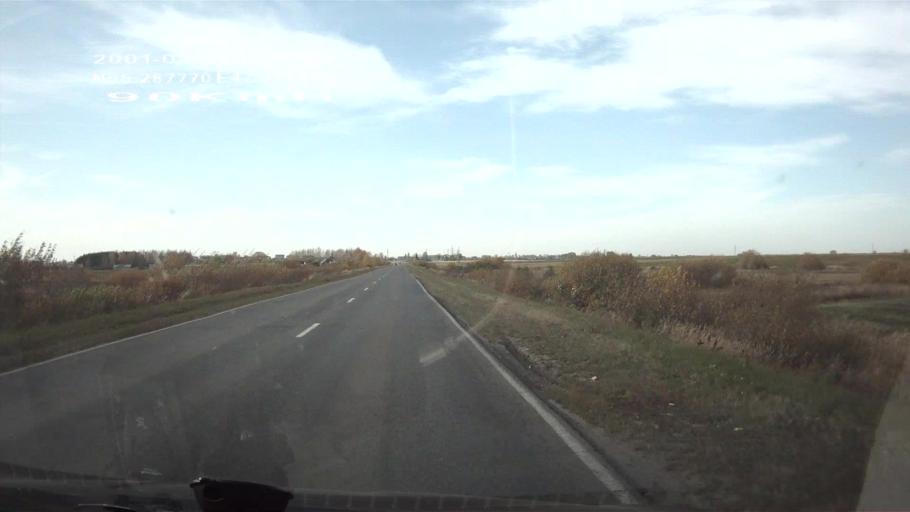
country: RU
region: Chuvashia
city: Ibresi
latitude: 55.2878
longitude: 47.0730
